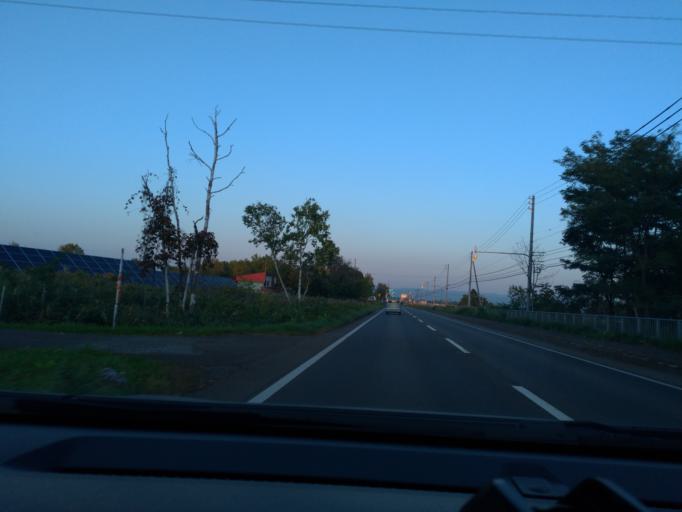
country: JP
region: Hokkaido
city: Tobetsu
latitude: 43.3276
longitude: 141.6436
